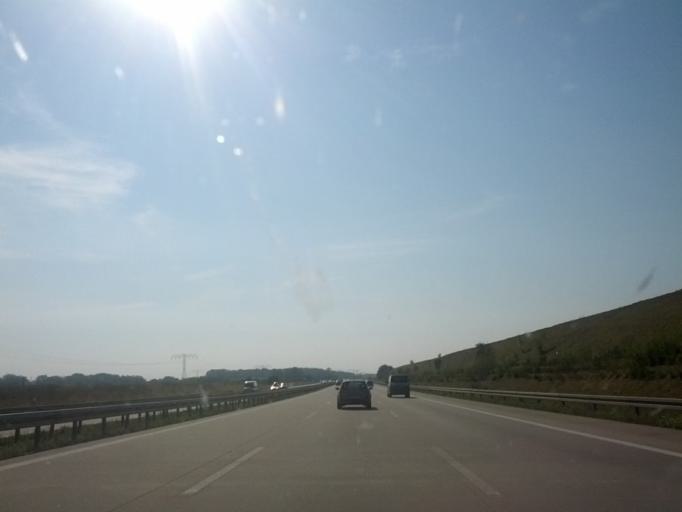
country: DE
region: Brandenburg
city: Neuenhagen
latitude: 52.5329
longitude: 13.7053
